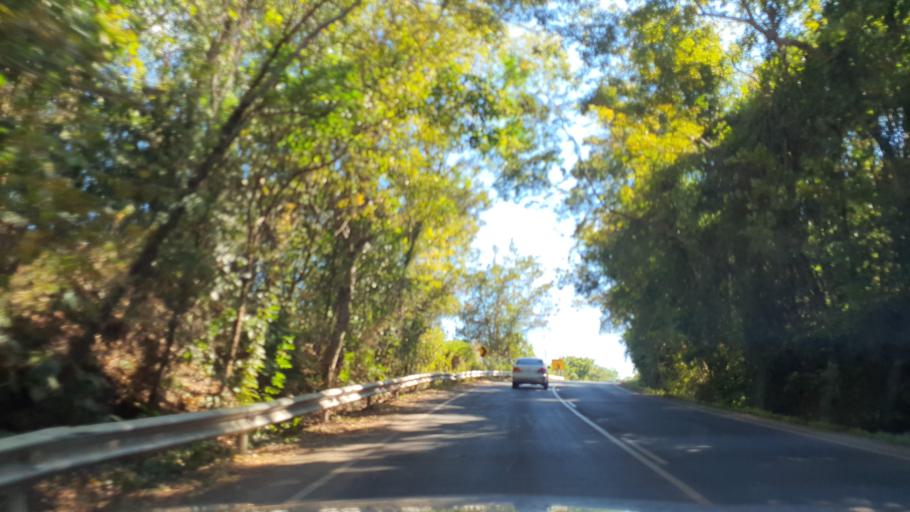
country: TH
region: Kalasin
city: Khao Wong
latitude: 16.7709
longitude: 104.1542
